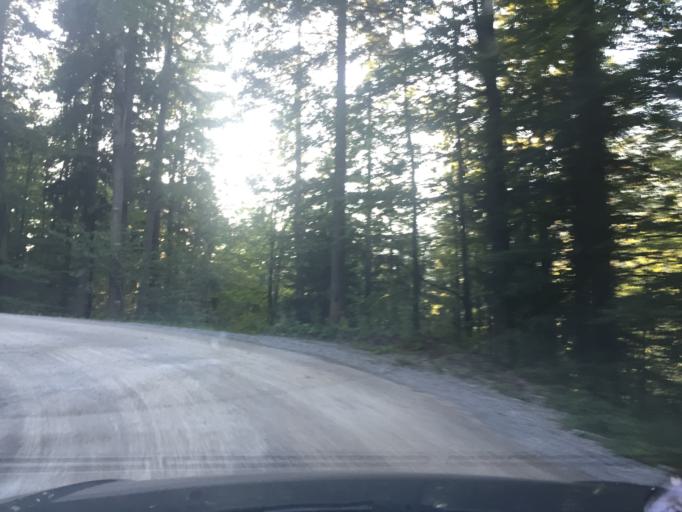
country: SI
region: Ravne na Koroskem
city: Kotlje
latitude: 46.4686
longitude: 14.9869
